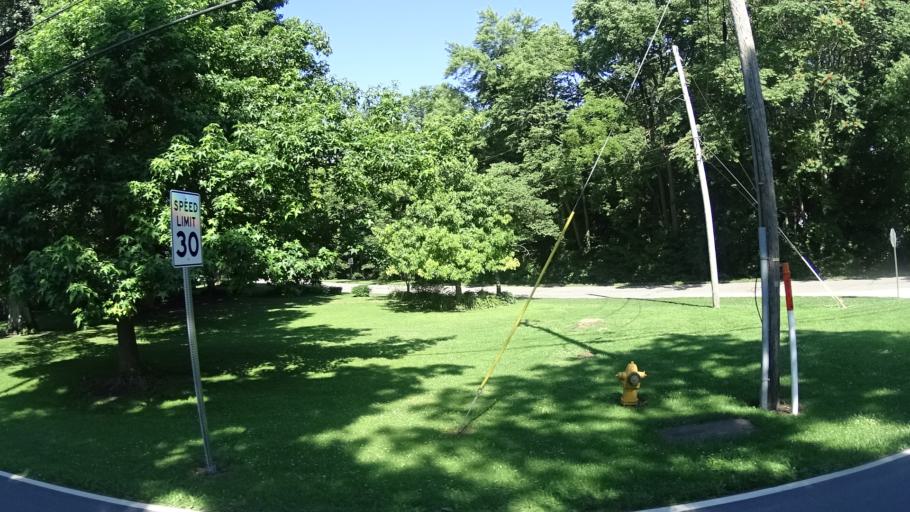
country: US
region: Indiana
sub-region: Madison County
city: Pendleton
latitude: 39.9897
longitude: -85.7496
